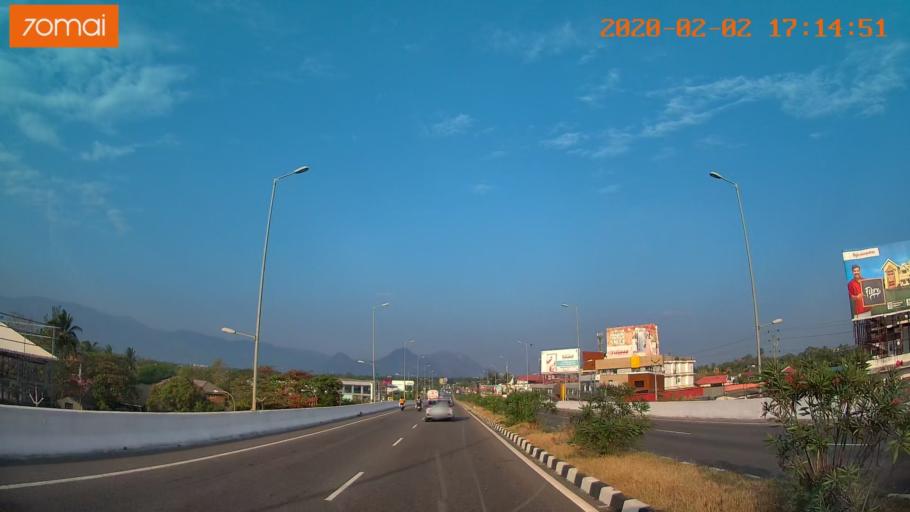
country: IN
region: Kerala
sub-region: Palakkad district
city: Palakkad
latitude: 10.7602
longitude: 76.6708
